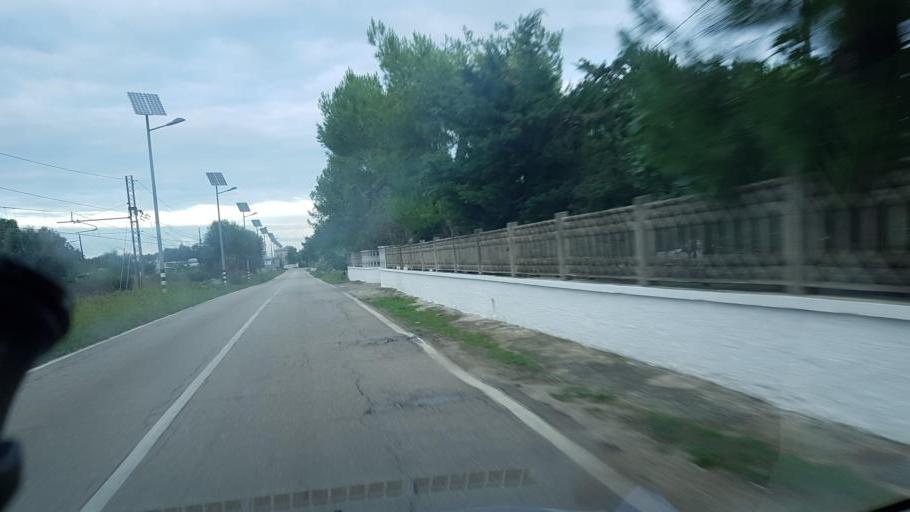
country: IT
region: Apulia
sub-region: Provincia di Brindisi
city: Latiano
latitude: 40.5417
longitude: 17.6969
